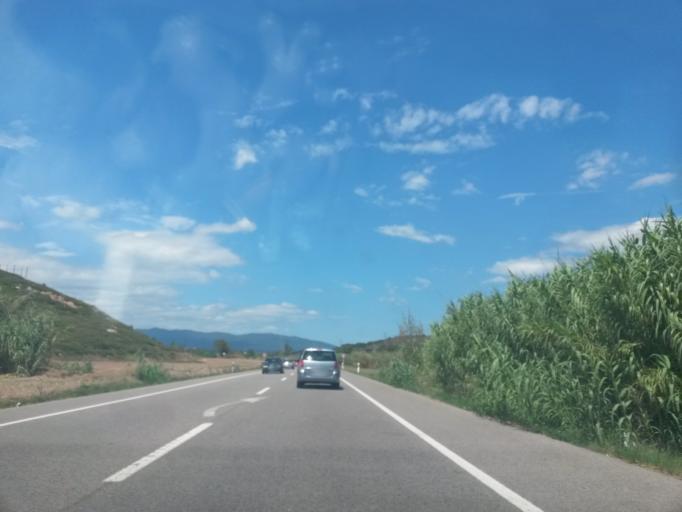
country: ES
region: Catalonia
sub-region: Provincia de Girona
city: Biure
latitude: 42.3445
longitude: 2.9146
